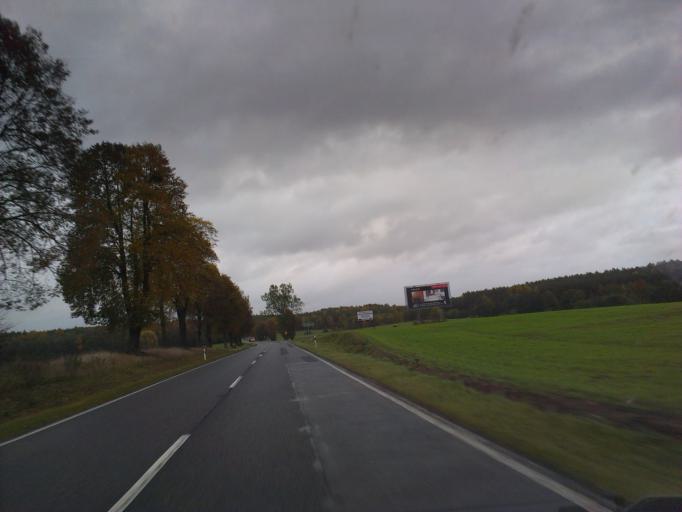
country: PL
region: Kujawsko-Pomorskie
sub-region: Powiat swiecki
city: Bukowiec
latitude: 53.4478
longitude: 18.2517
